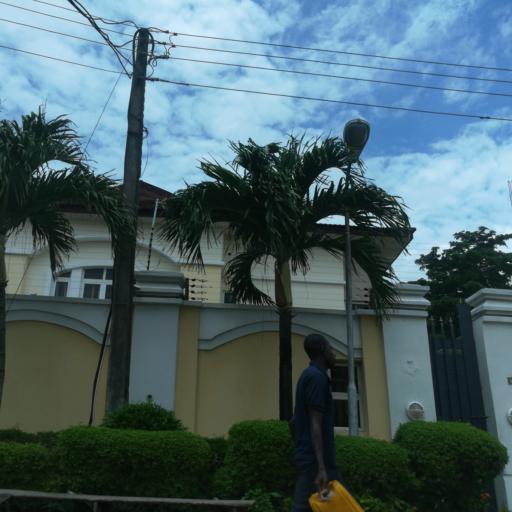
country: NG
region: Lagos
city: Ikoyi
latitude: 6.4448
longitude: 3.4614
